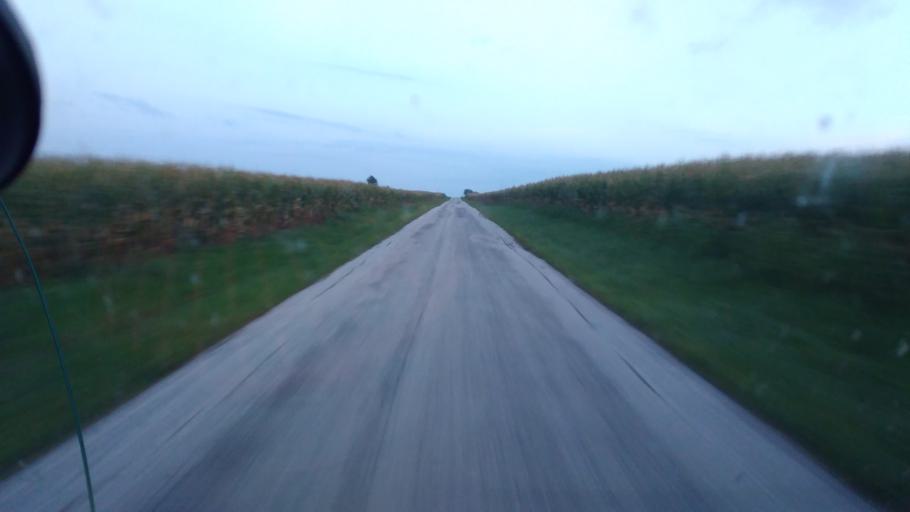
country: US
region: Ohio
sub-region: Hardin County
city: Kenton
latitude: 40.6503
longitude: -83.4585
